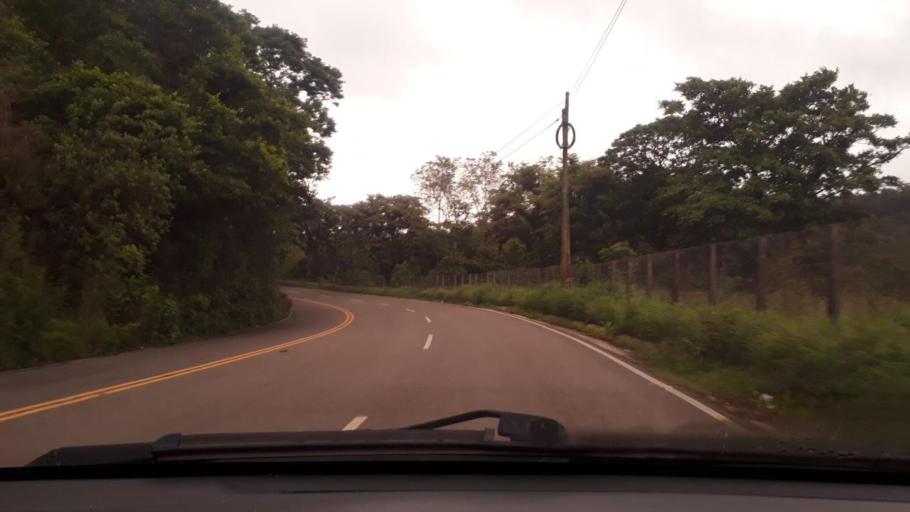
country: GT
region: Chiquimula
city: Esquipulas
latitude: 14.5632
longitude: -89.3632
